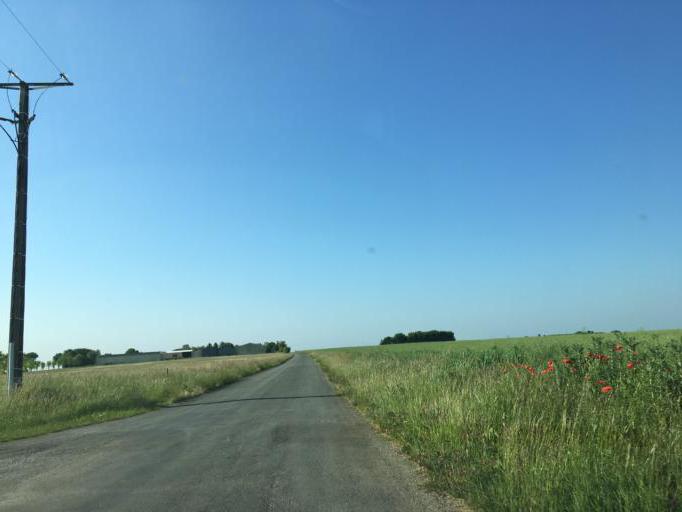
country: FR
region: Poitou-Charentes
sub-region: Departement des Deux-Sevres
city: Beauvoir-sur-Niort
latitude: 46.0884
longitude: -0.5063
